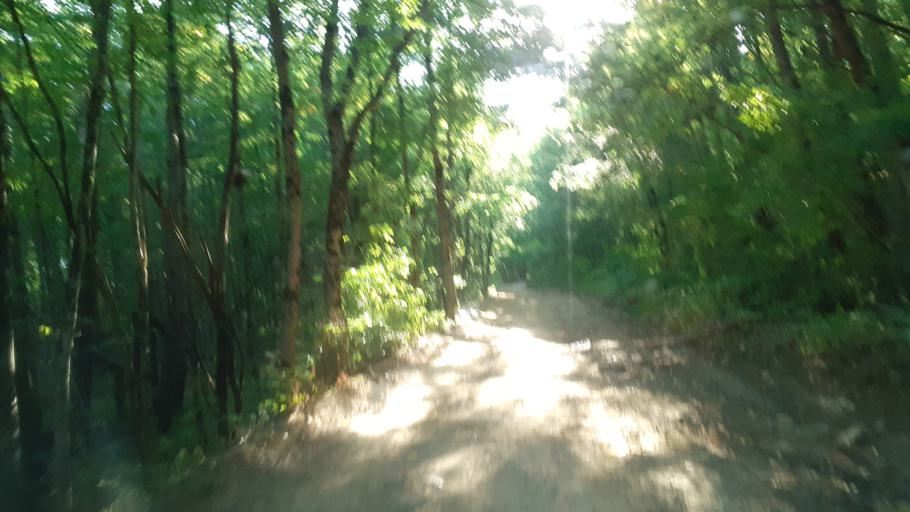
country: RU
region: Krasnodarskiy
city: Azovskaya
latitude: 44.6638
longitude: 38.4916
